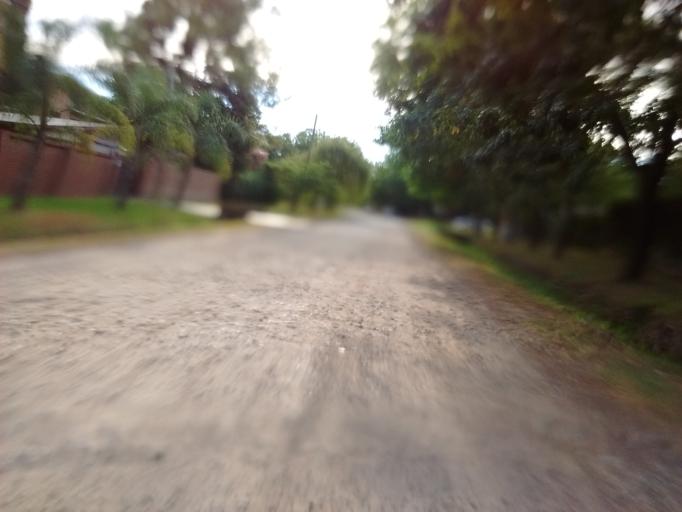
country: AR
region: Santa Fe
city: Funes
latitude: -32.9259
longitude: -60.8109
